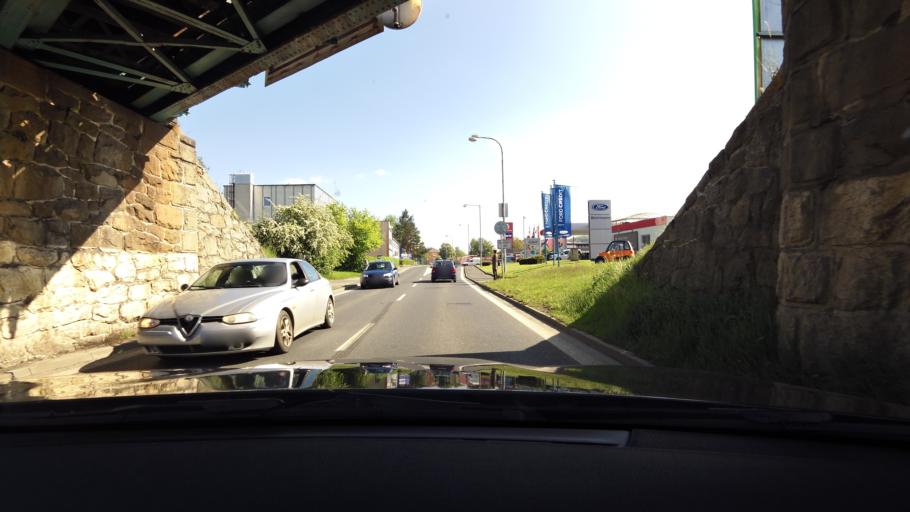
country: CZ
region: Plzensky
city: Klatovy
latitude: 49.3855
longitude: 13.2968
